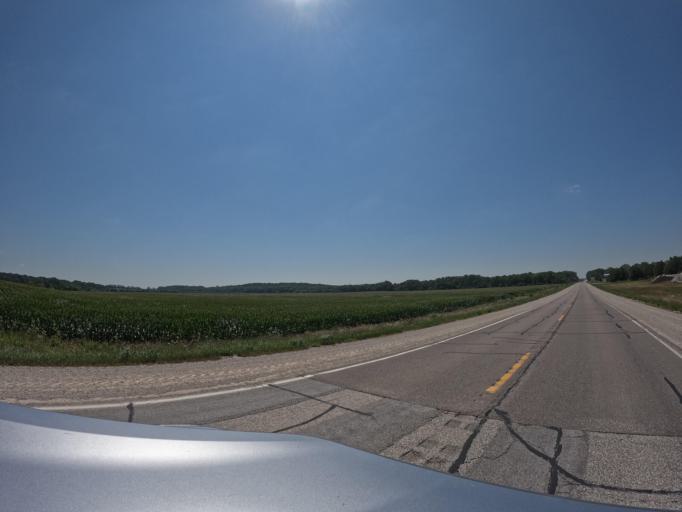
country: US
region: Iowa
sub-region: Keokuk County
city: Sigourney
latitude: 41.3146
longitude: -92.2051
